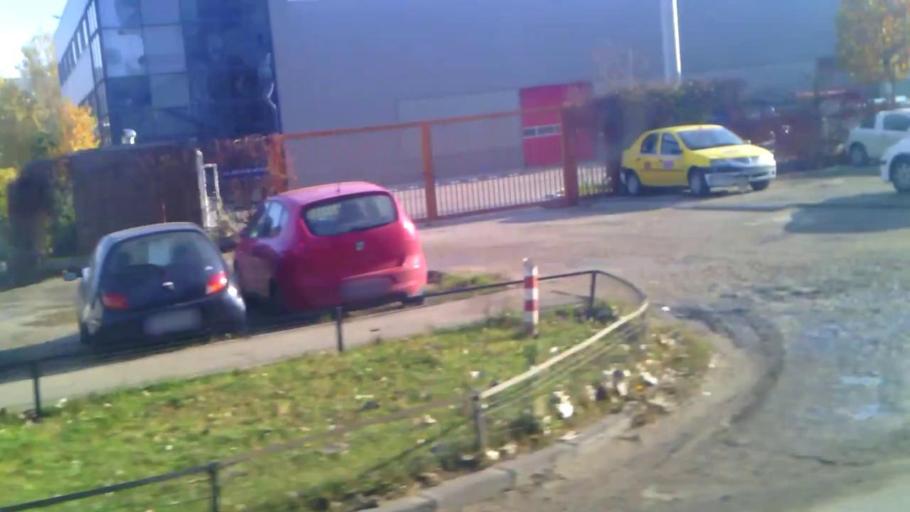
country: RO
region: Ilfov
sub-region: Comuna Popesti-Leordeni
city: Popesti-Leordeni
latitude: 44.3656
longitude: 26.1459
